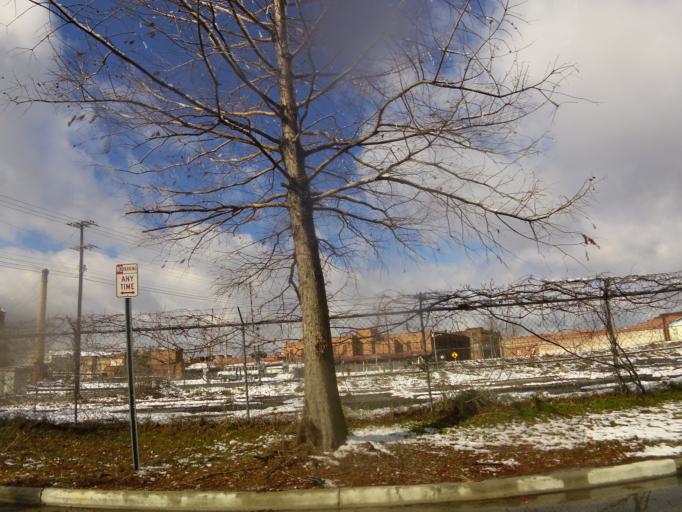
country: US
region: North Carolina
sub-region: Wilson County
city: Wilson
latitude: 35.7211
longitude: -77.9082
